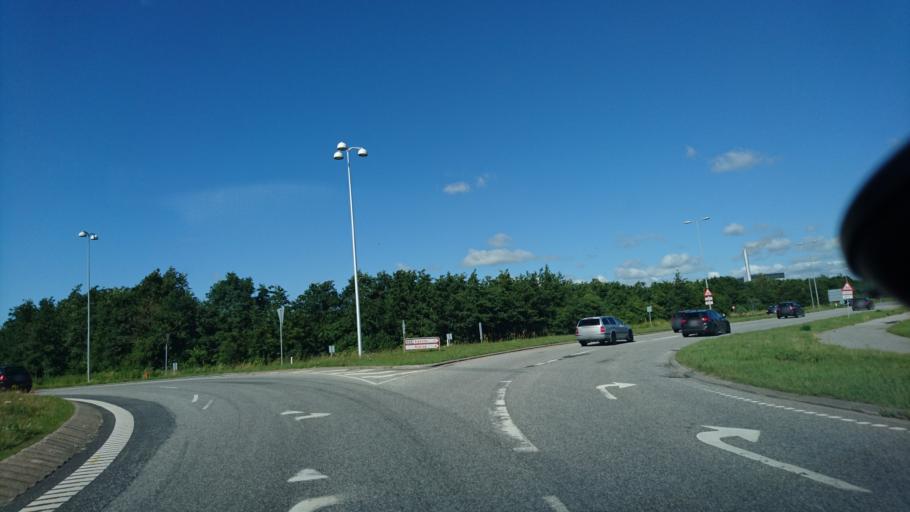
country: DK
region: North Denmark
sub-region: Alborg Kommune
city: Gistrup
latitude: 57.0201
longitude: 10.0054
